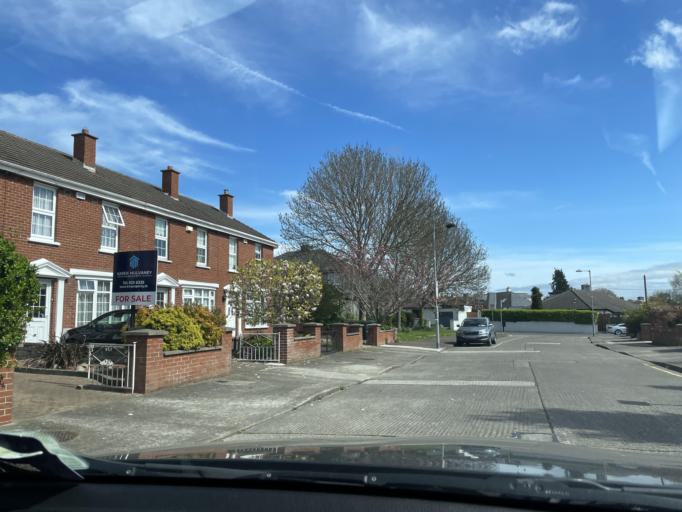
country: IE
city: Killester
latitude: 53.3739
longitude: -6.2067
